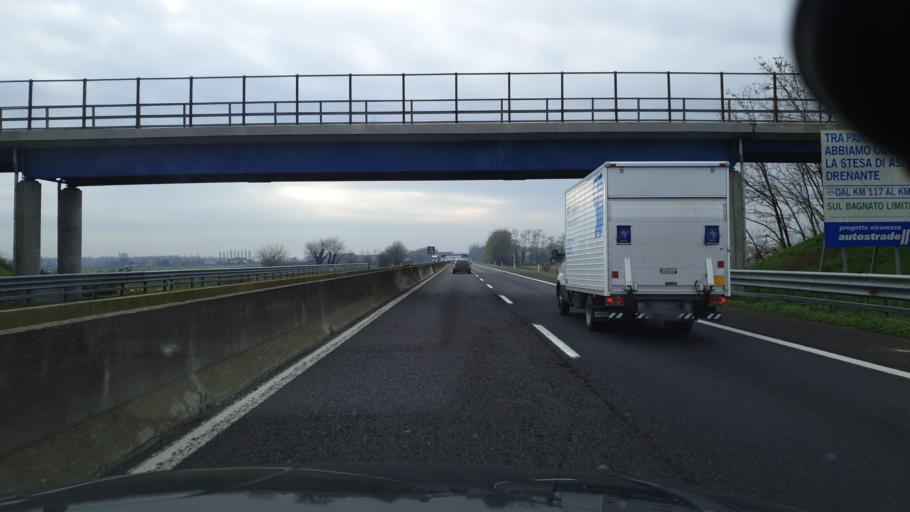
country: IT
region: Veneto
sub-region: Provincia di Padova
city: Monselice
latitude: 45.2268
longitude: 11.7746
